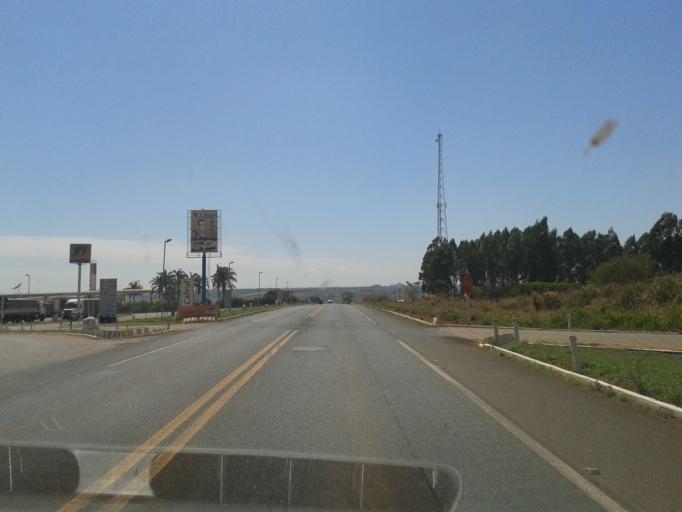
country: BR
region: Minas Gerais
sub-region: Sacramento
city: Sacramento
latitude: -19.3180
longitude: -47.5483
